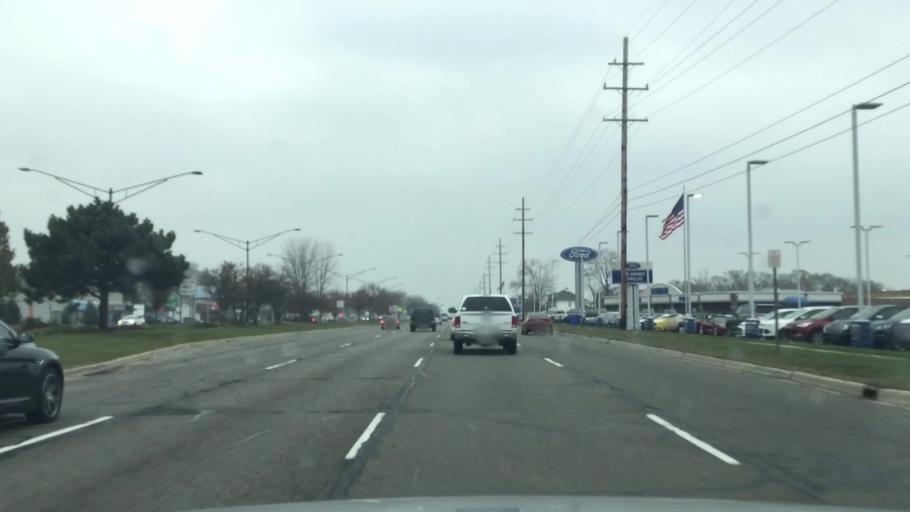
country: US
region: Michigan
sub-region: Macomb County
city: Clinton
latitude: 42.5606
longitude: -82.8963
